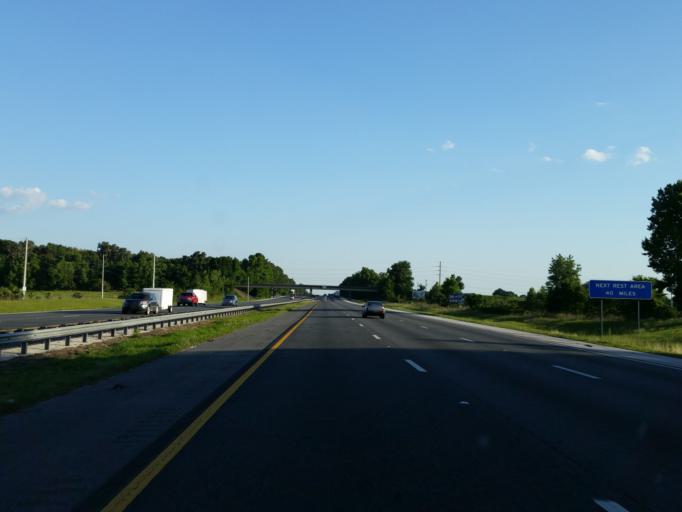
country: US
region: Florida
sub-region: Marion County
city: Ocala
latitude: 29.1246
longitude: -82.1849
